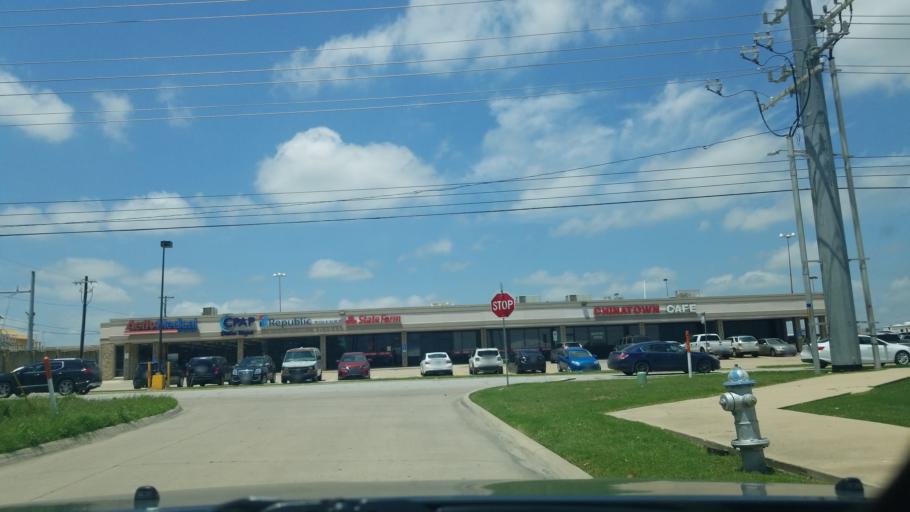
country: US
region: Texas
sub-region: Denton County
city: Denton
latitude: 33.2282
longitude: -97.1607
